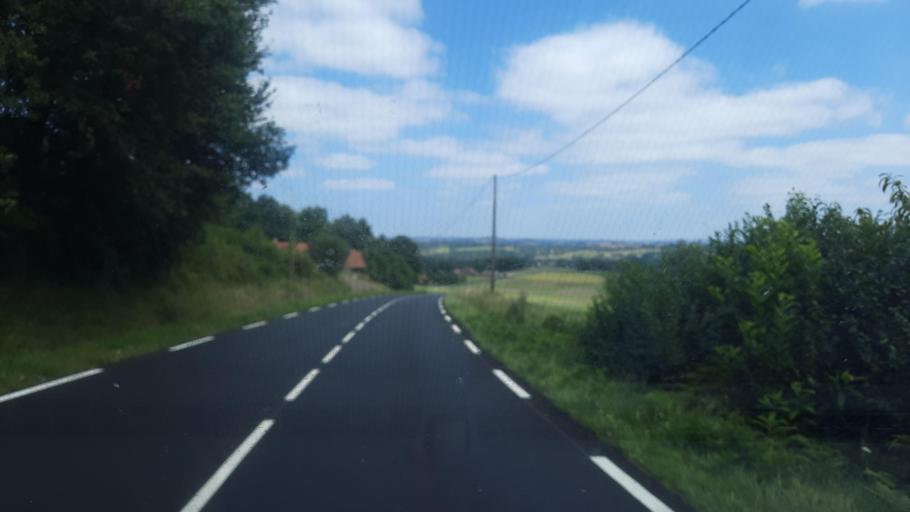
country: FR
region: Midi-Pyrenees
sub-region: Departement de la Haute-Garonne
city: Boulogne-sur-Gesse
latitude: 43.2997
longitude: 0.5999
